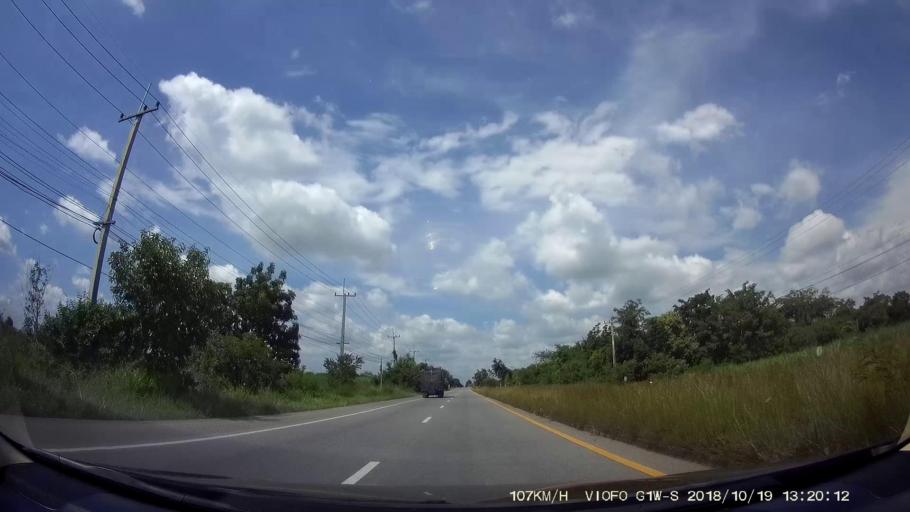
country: TH
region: Chaiyaphum
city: Chatturat
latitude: 15.4420
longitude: 101.8291
